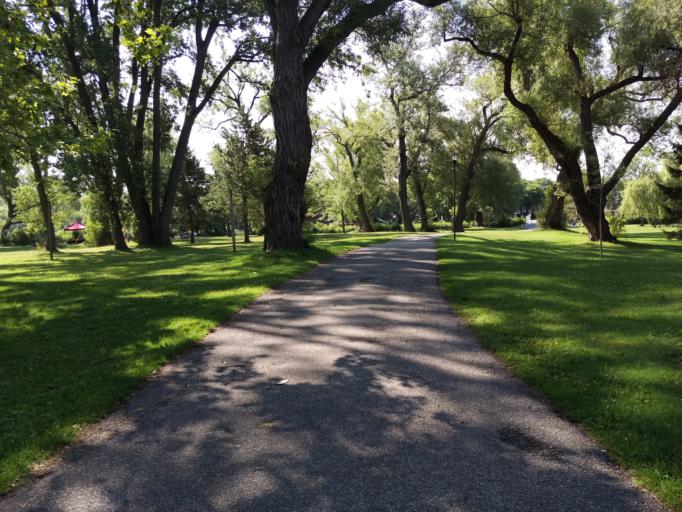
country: CA
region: Ontario
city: Toronto
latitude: 43.6226
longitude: -79.3734
